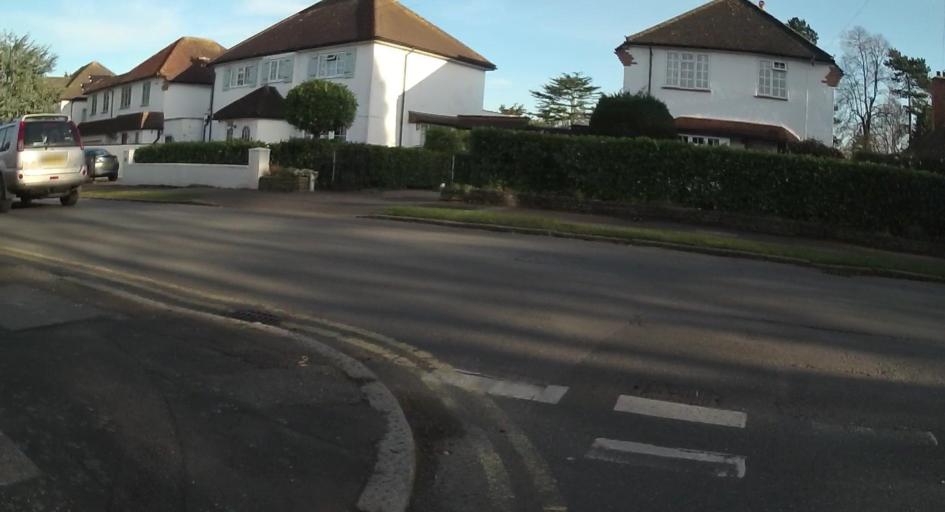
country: GB
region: England
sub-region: Surrey
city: Walton-on-Thames
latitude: 51.3814
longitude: -0.4105
